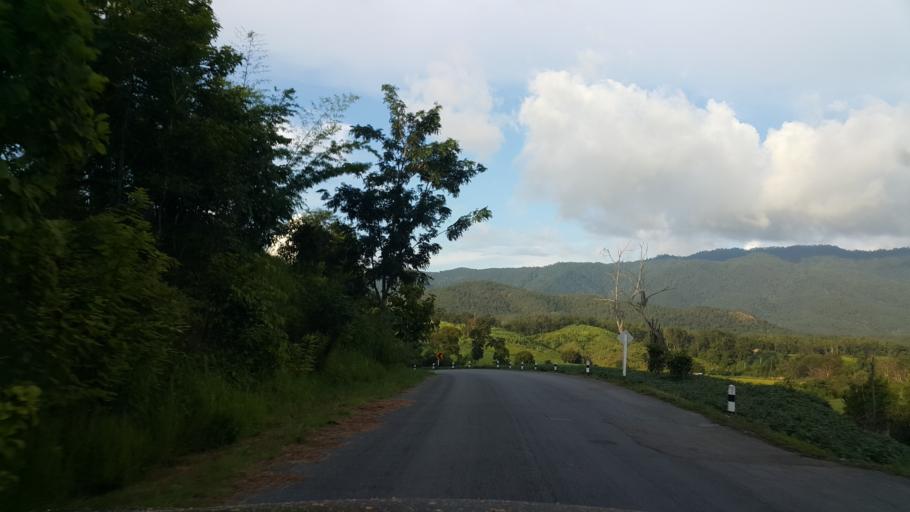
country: TH
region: Mae Hong Son
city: Mae Hi
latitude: 19.1927
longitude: 98.4200
